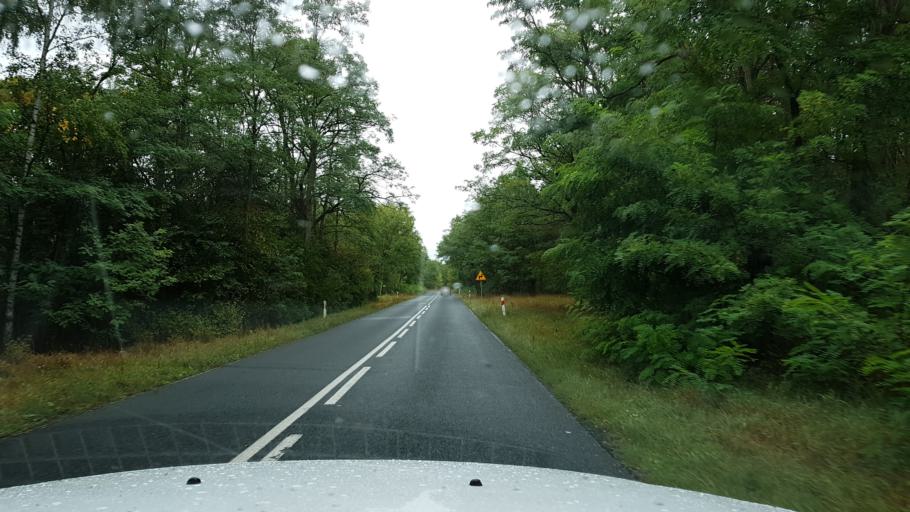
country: PL
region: West Pomeranian Voivodeship
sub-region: Powiat gryfinski
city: Cedynia
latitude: 52.8384
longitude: 14.1276
